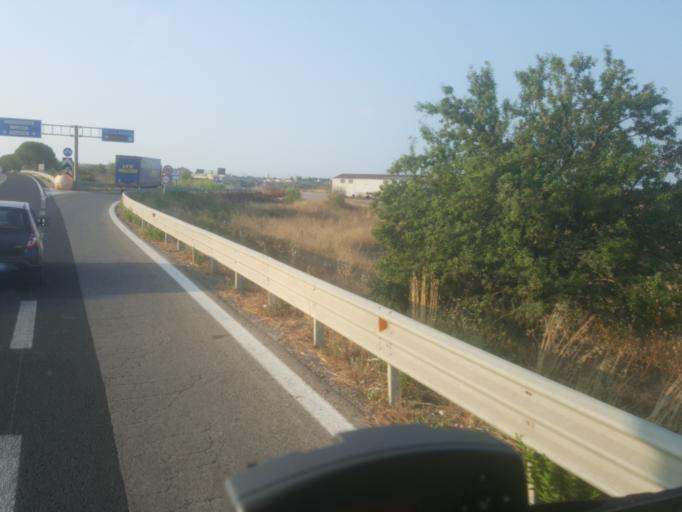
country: IT
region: Latium
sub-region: Citta metropolitana di Roma Capitale
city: Aurelia
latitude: 42.1578
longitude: 11.7892
